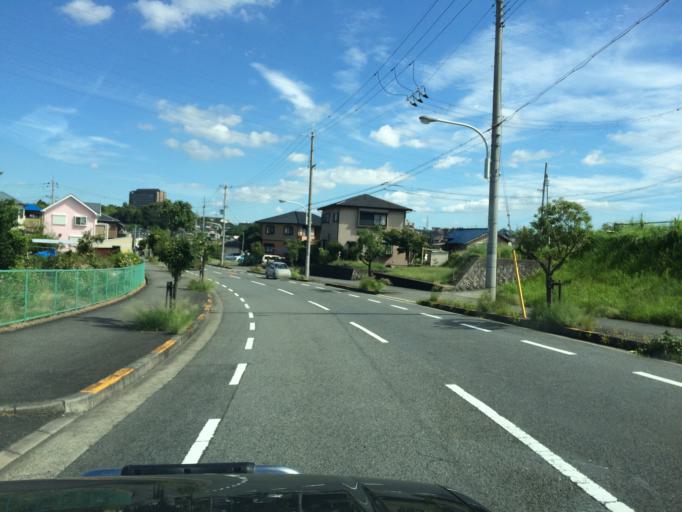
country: JP
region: Osaka
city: Izumi
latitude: 34.4431
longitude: 135.4497
